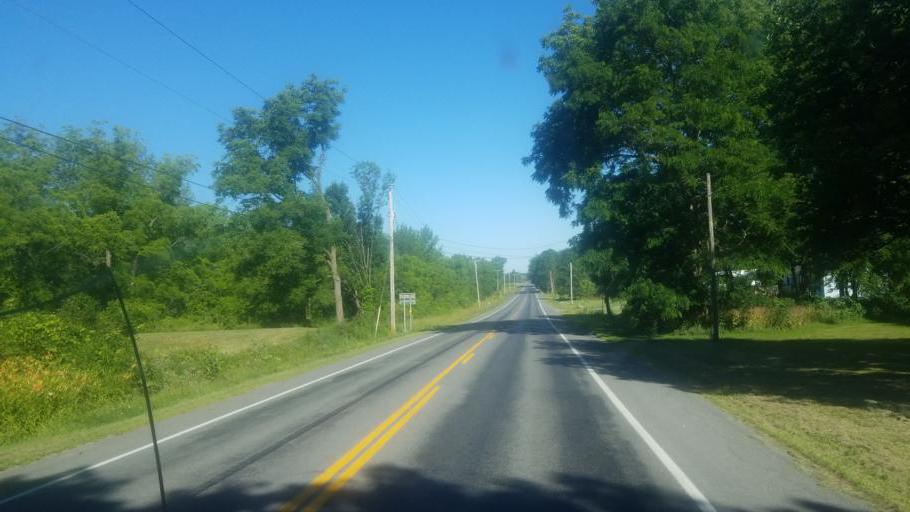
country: US
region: New York
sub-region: Ontario County
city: Canandaigua
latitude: 42.8369
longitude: -77.2156
